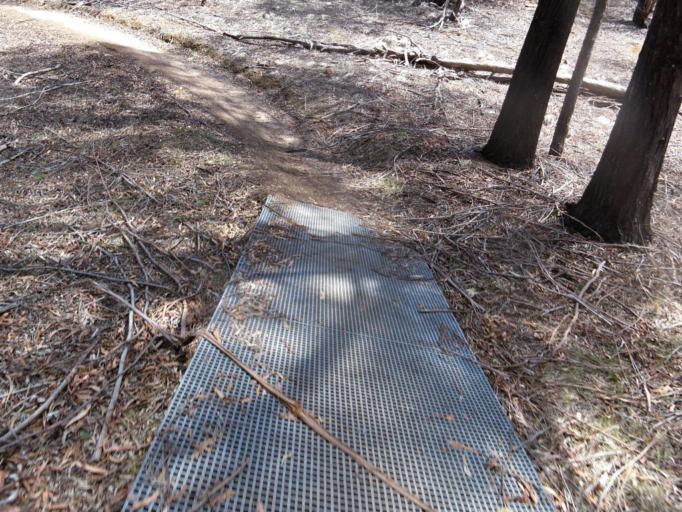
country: AU
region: Australian Capital Territory
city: Kaleen
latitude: -35.1374
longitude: 149.1418
